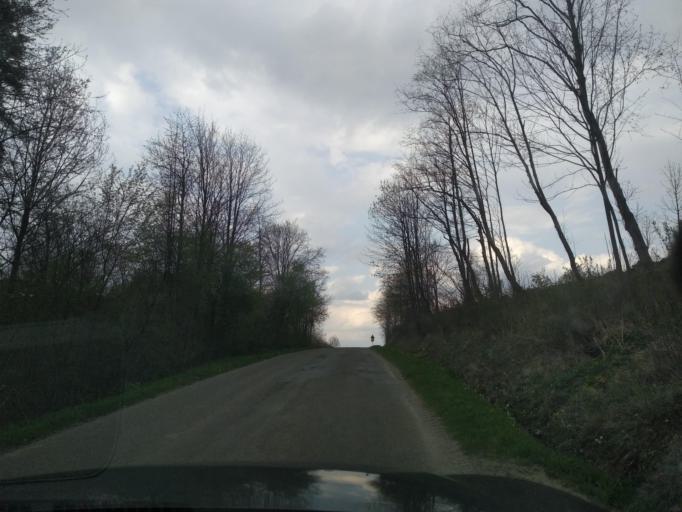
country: PL
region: Subcarpathian Voivodeship
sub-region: Powiat sanocki
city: Czaszyn
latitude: 49.3894
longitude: 22.2083
